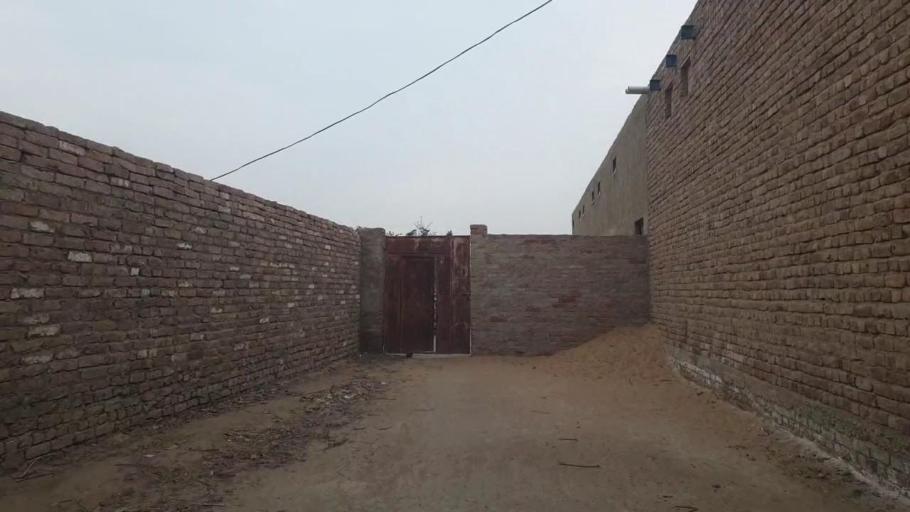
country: PK
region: Sindh
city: Tando Adam
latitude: 25.7754
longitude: 68.6460
